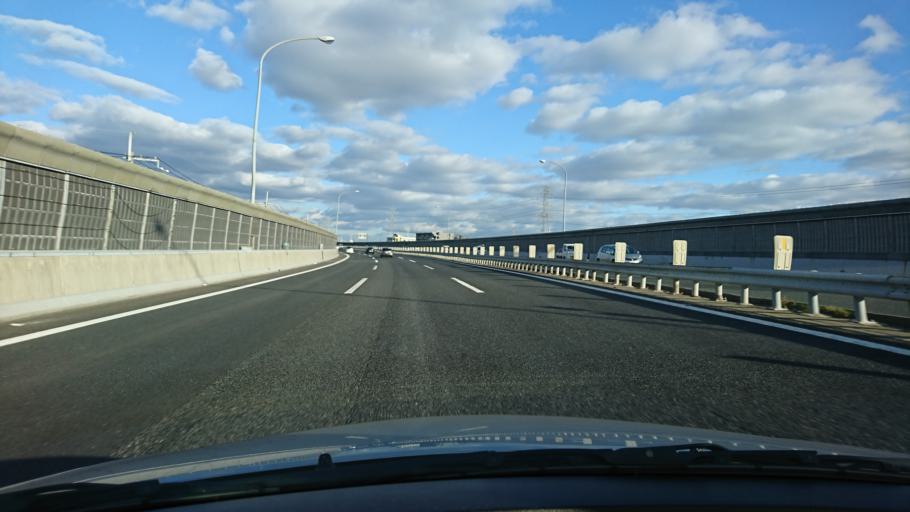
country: JP
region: Hyogo
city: Takarazuka
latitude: 34.8054
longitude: 135.3745
